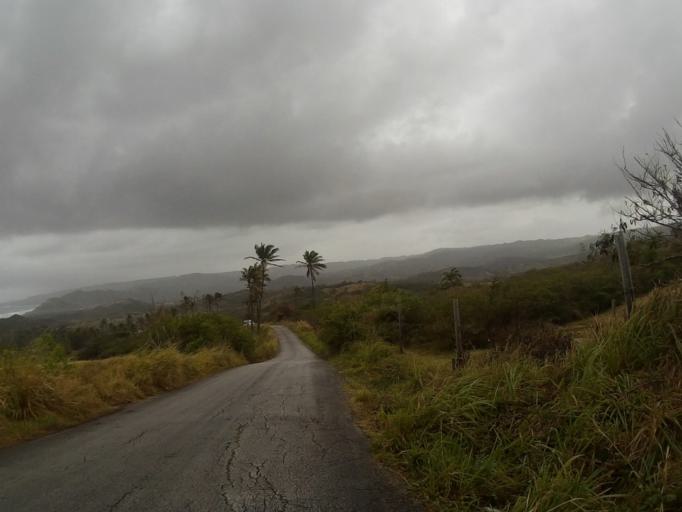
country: BB
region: Saint Andrew
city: Greenland
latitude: 13.2717
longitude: -59.5772
